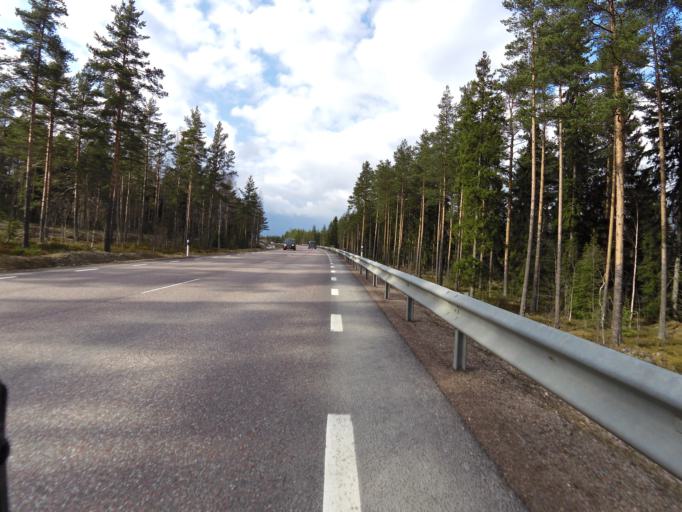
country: SE
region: Gaevleborg
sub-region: Hofors Kommun
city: Hofors
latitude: 60.4906
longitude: 16.4419
